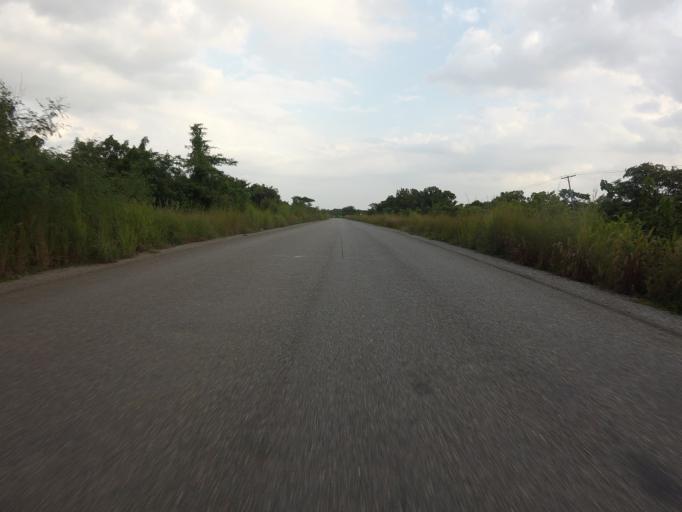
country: GH
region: Volta
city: Ho
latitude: 6.4326
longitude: 0.5068
